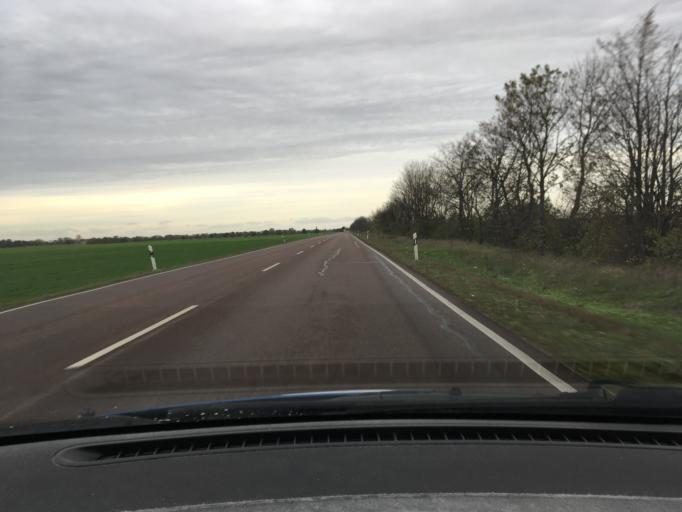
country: DE
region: Saxony-Anhalt
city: Zerbst
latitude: 51.9814
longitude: 12.0569
